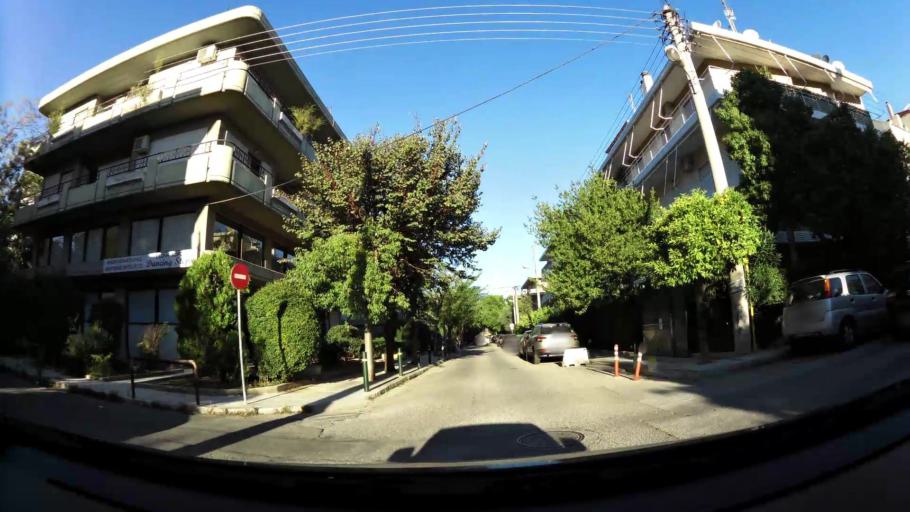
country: GR
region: Attica
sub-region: Nomarchia Athinas
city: Neo Psychiko
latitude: 38.0091
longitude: 23.7906
